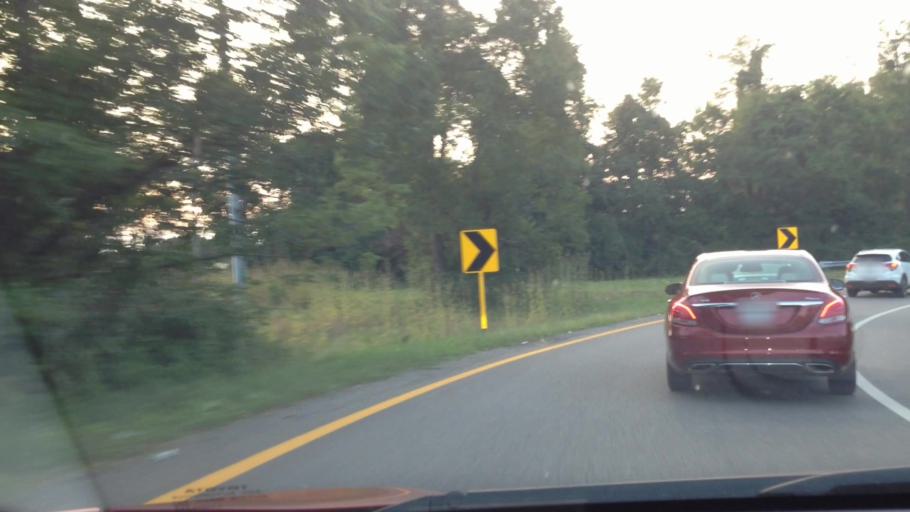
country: US
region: Ohio
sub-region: Summit County
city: Montrose-Ghent
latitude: 41.1363
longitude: -81.6536
